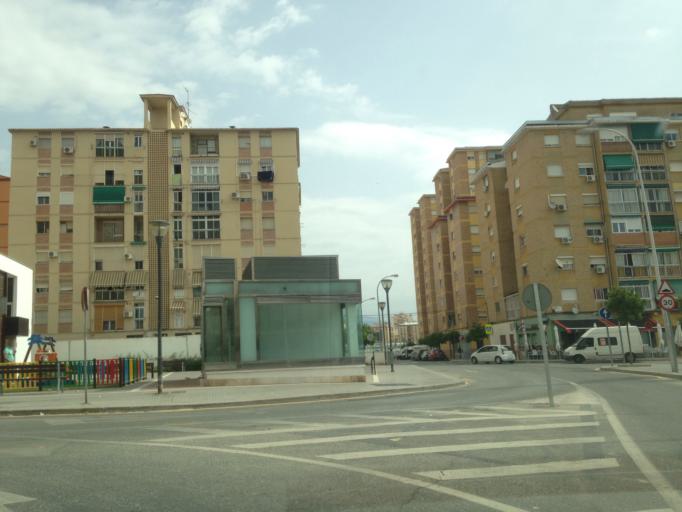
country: ES
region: Andalusia
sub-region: Provincia de Malaga
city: Malaga
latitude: 36.7084
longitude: -4.4423
